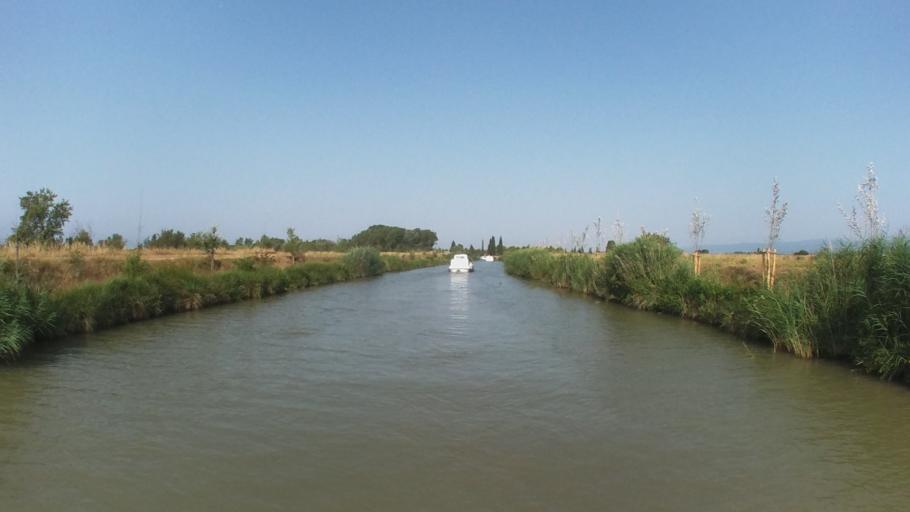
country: FR
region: Languedoc-Roussillon
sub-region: Departement de l'Herault
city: Olonzac
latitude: 43.2668
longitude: 2.7094
